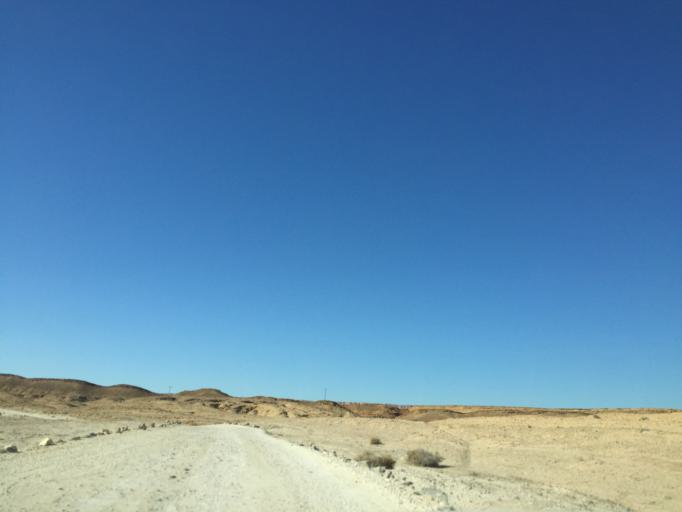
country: IL
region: Southern District
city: Mitzpe Ramon
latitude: 30.6145
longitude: 34.9068
